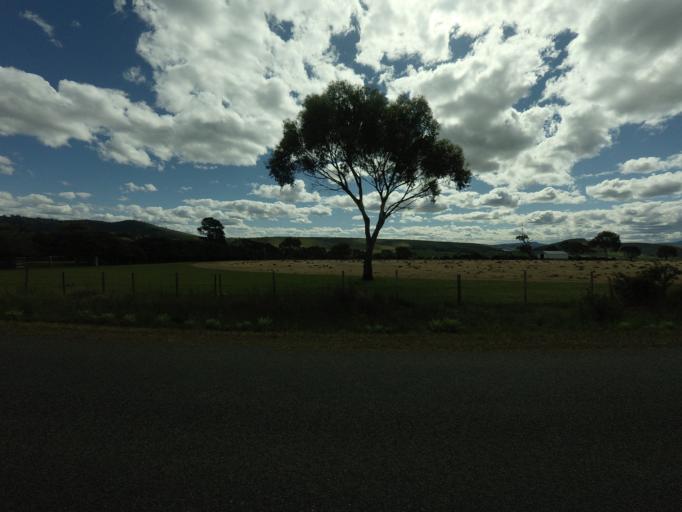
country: AU
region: Tasmania
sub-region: Brighton
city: Bridgewater
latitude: -42.3935
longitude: 147.3148
